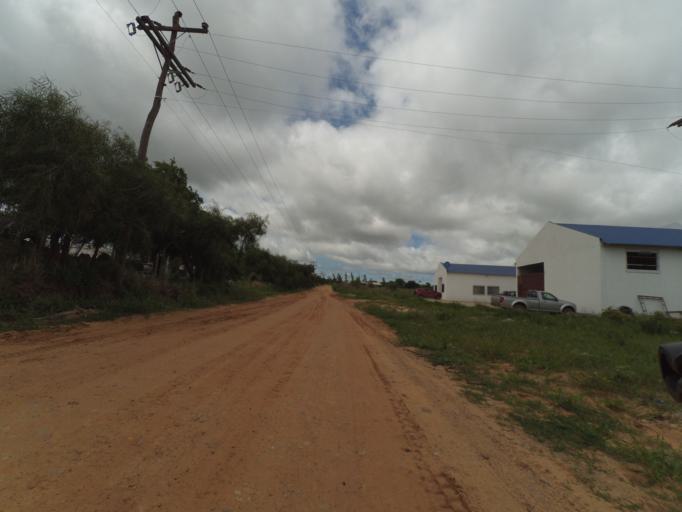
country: BO
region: Santa Cruz
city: Santa Rita
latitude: -17.9110
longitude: -63.2492
